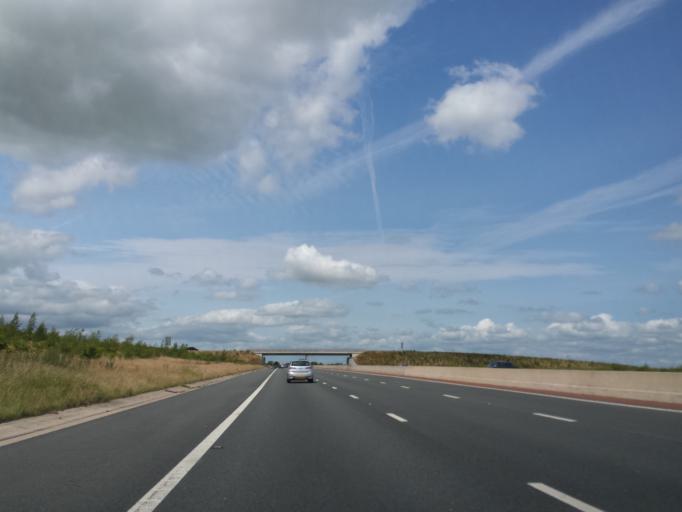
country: GB
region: England
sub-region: North Yorkshire
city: Ripon
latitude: 54.2366
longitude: -1.4972
